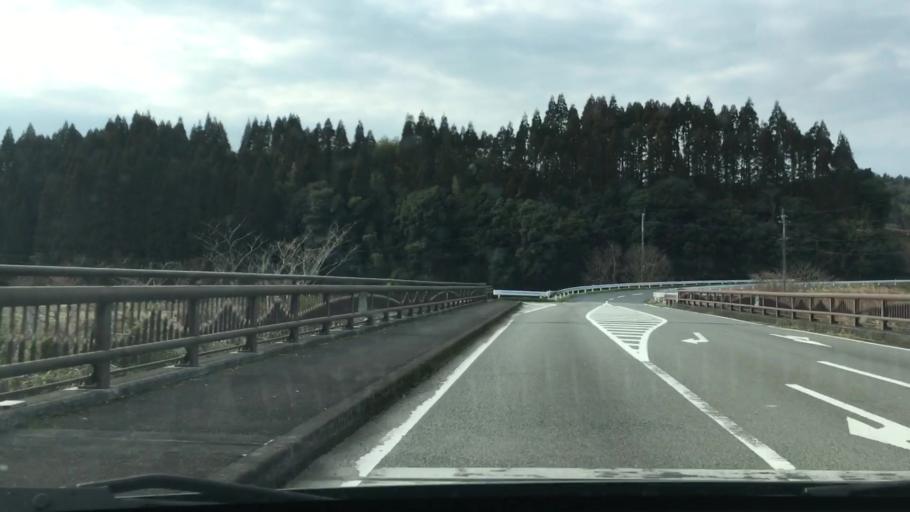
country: JP
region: Miyazaki
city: Nichinan
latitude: 31.6164
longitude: 131.3366
